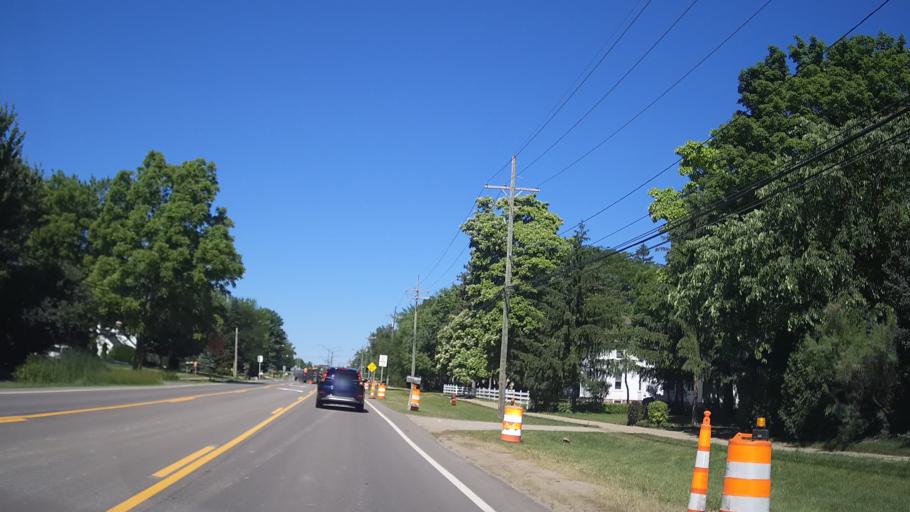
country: US
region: Michigan
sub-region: Oakland County
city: Troy
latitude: 42.6063
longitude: -83.1555
